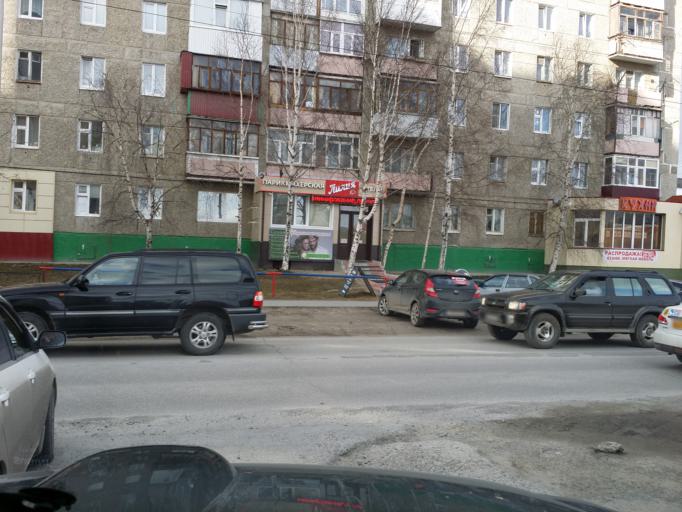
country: RU
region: Khanty-Mansiyskiy Avtonomnyy Okrug
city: Nizhnevartovsk
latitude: 60.9399
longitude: 76.5991
